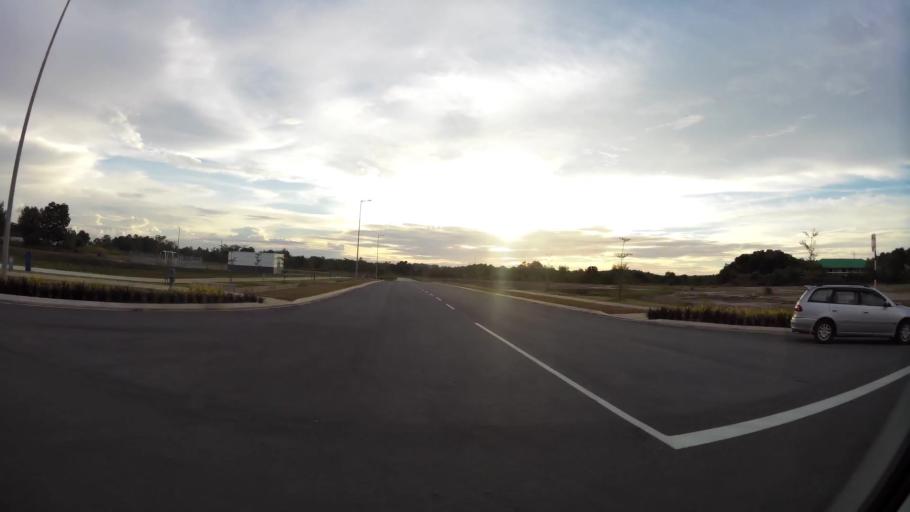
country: BN
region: Brunei and Muara
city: Bandar Seri Begawan
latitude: 4.9893
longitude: 114.9830
